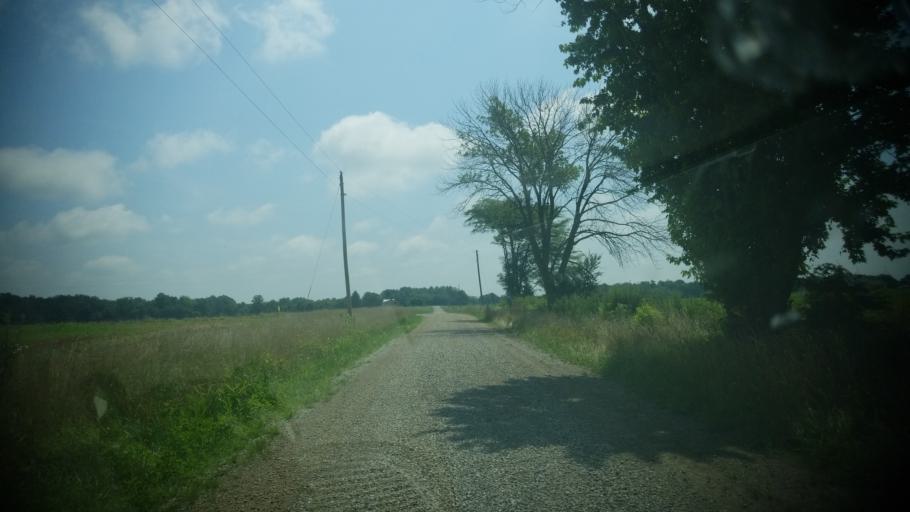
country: US
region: Illinois
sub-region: Wayne County
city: Fairfield
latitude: 38.5297
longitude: -88.3713
